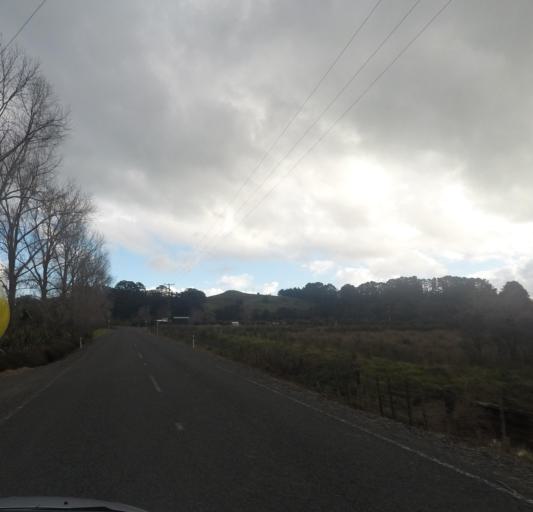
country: NZ
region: Auckland
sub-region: Auckland
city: Warkworth
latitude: -36.3745
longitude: 174.7977
